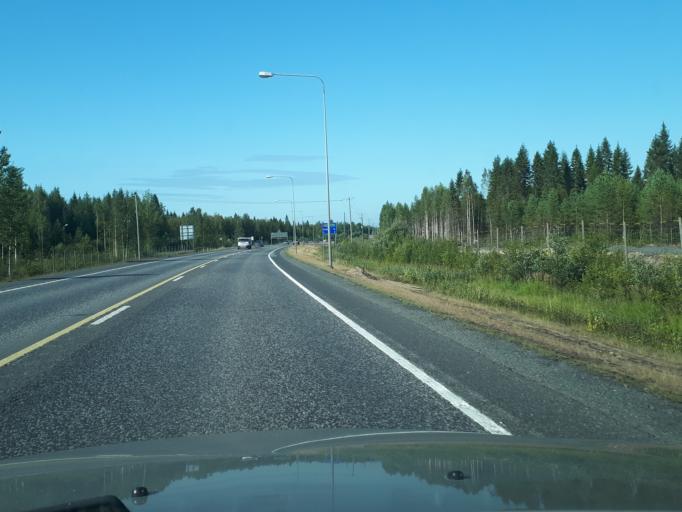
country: FI
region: Northern Ostrobothnia
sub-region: Oulunkaari
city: Ii
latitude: 65.2671
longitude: 25.3629
